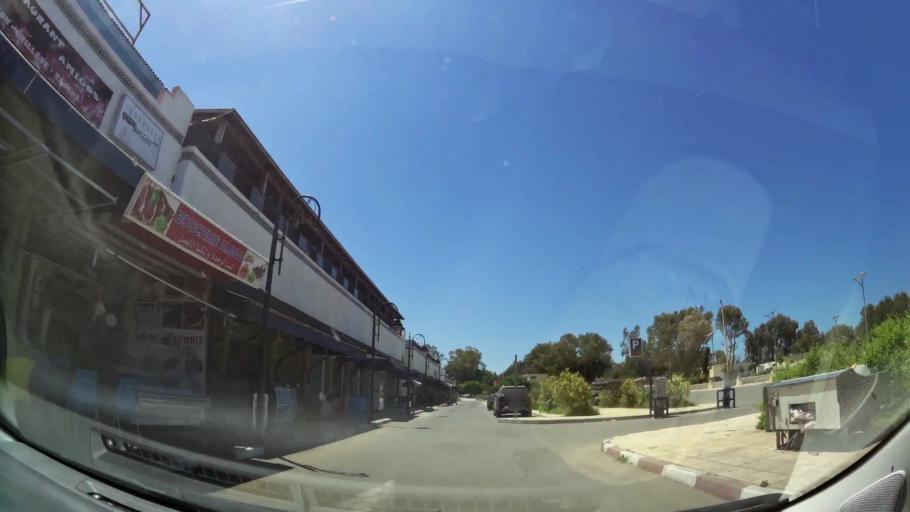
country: MA
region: Oriental
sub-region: Berkane-Taourirt
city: Madagh
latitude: 35.0813
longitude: -2.2138
